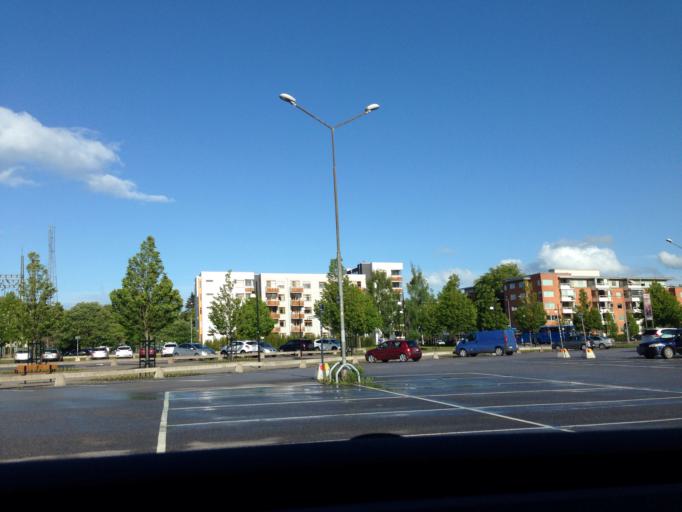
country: SE
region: Vaestra Goetaland
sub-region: Skovde Kommun
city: Skoevde
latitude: 58.3922
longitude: 13.8393
